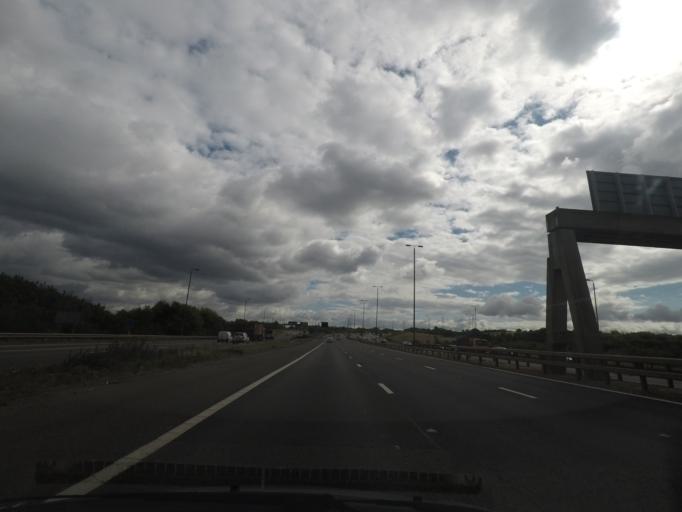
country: GB
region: England
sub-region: City and Borough of Leeds
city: Lofthouse
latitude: 53.7408
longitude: -1.5137
